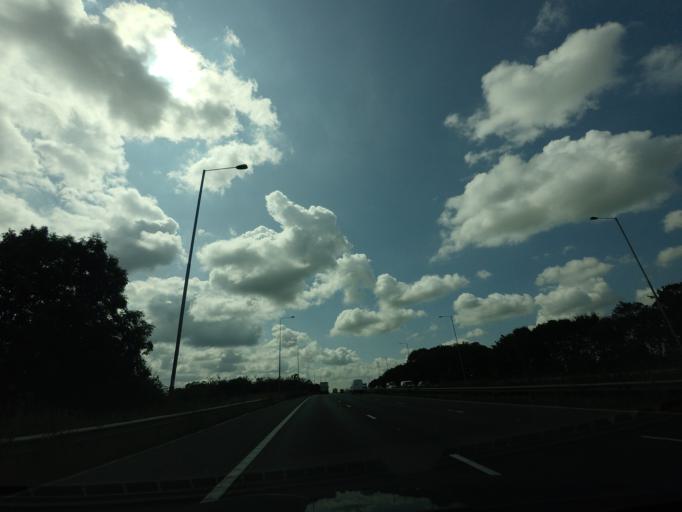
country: GB
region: England
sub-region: Lancashire
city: Leyland
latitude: 53.6864
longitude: -2.6790
